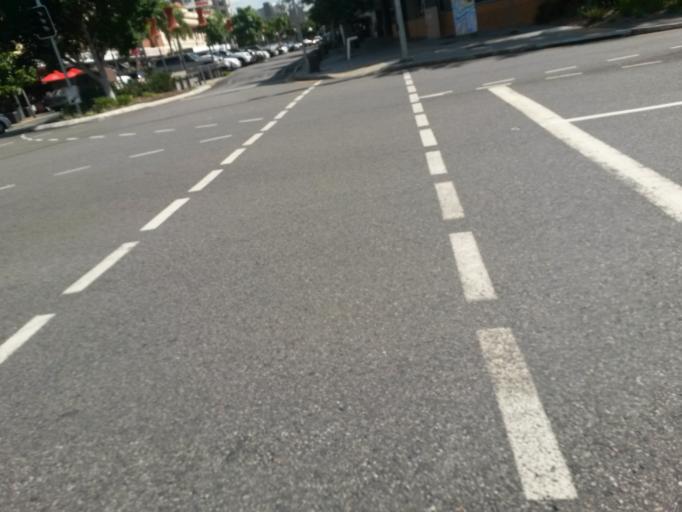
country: AU
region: Queensland
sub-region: Brisbane
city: Woolloongabba
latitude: -27.4876
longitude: 153.0374
